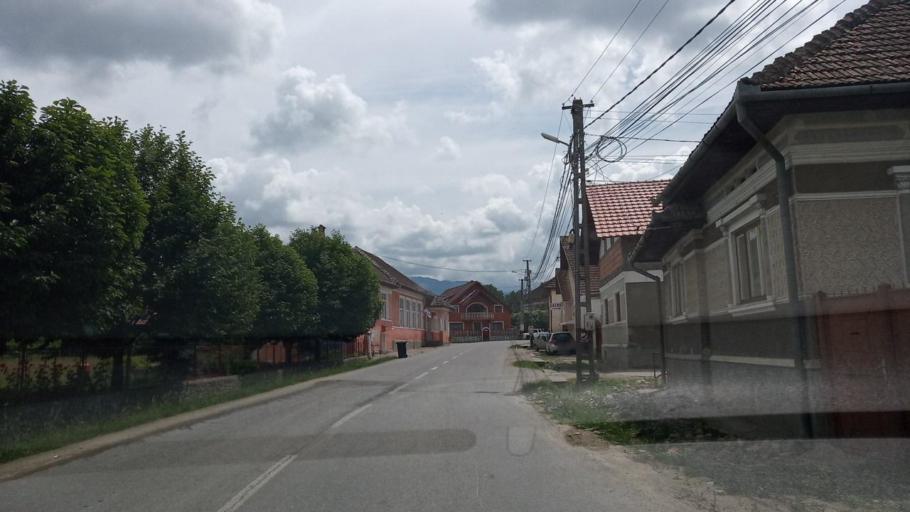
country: RO
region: Sibiu
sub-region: Comuna Cartisoara
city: Cartisoara
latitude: 45.7274
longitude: 24.5768
